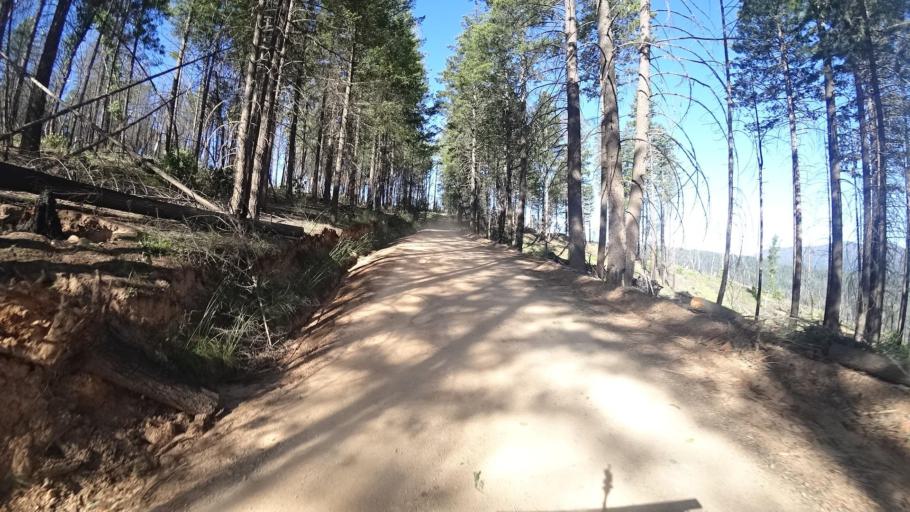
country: US
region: California
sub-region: Lake County
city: Upper Lake
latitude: 39.3864
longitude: -122.9824
